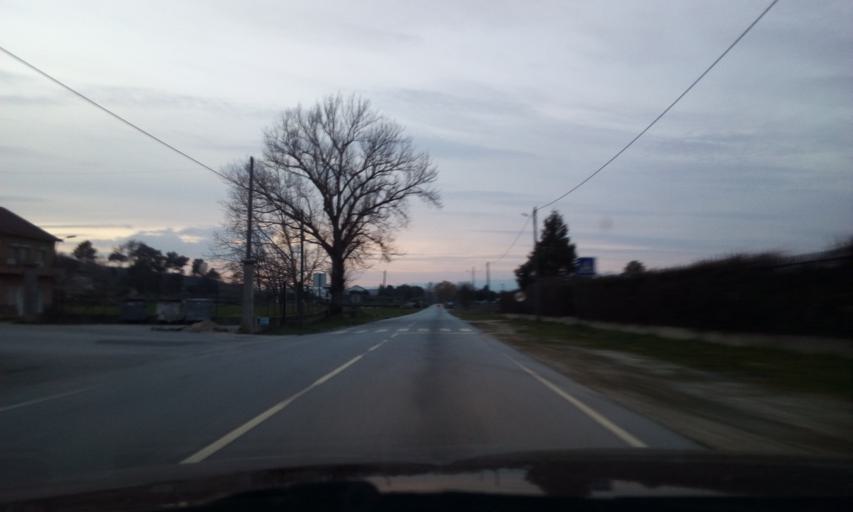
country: PT
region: Guarda
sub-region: Guarda
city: Guarda
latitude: 40.6134
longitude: -7.3052
